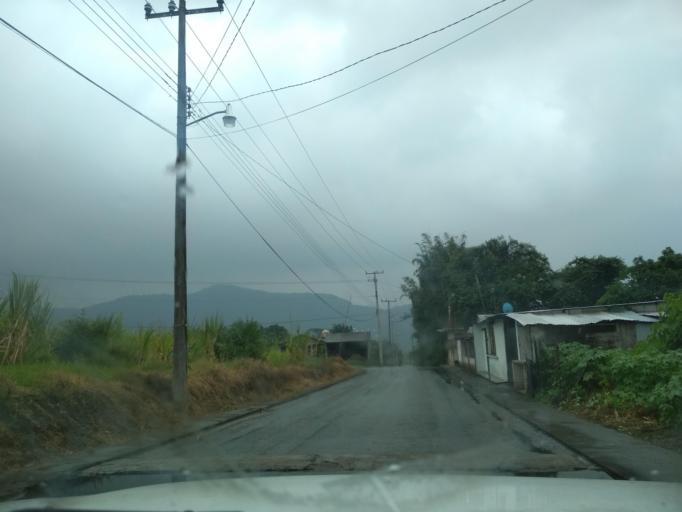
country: MX
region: Veracruz
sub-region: Mariano Escobedo
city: Chicola
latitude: 18.8989
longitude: -97.1184
